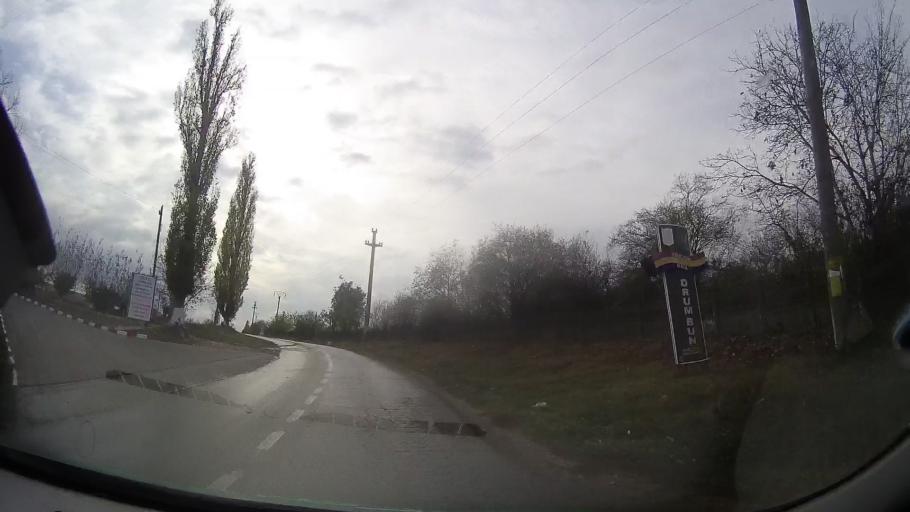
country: RO
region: Ialomita
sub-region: Comuna Maia
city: Maia
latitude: 44.7276
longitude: 26.3932
